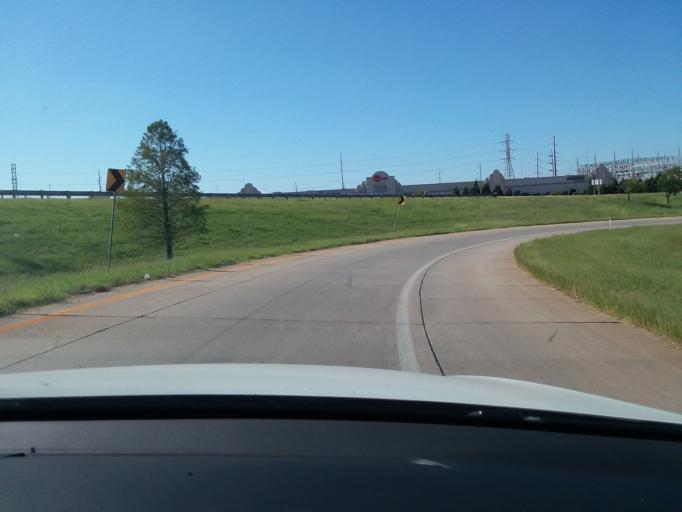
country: US
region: Oklahoma
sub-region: Oklahoma County
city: Edmond
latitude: 35.5985
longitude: -97.5027
